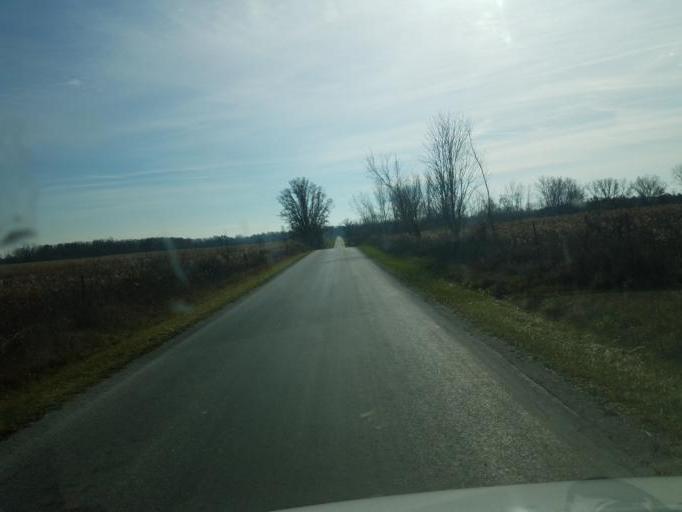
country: US
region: Ohio
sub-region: Hardin County
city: Kenton
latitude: 40.6206
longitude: -83.4386
